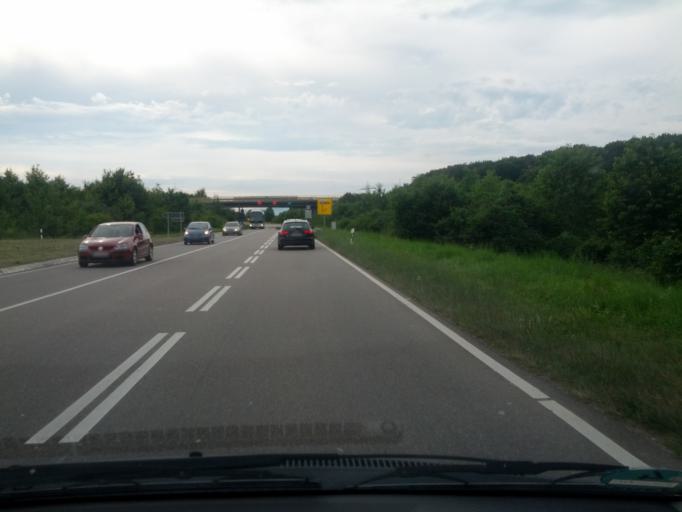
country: DE
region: Baden-Wuerttemberg
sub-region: Freiburg Region
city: Rust
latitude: 48.2584
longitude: 7.7497
